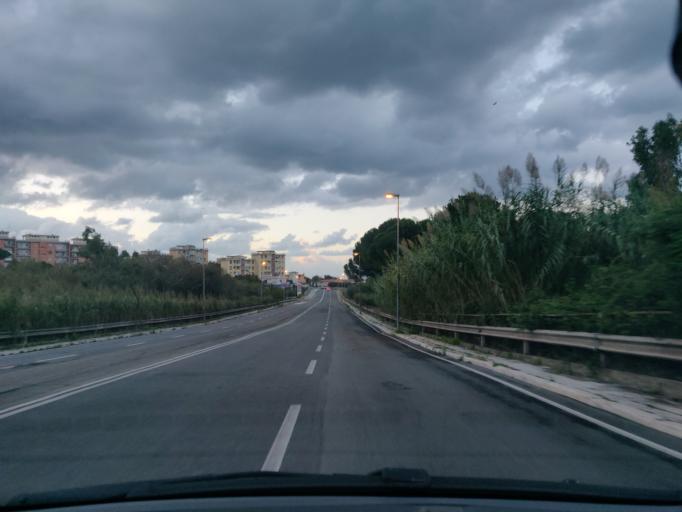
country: IT
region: Latium
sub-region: Citta metropolitana di Roma Capitale
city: Civitavecchia
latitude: 42.0842
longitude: 11.8087
